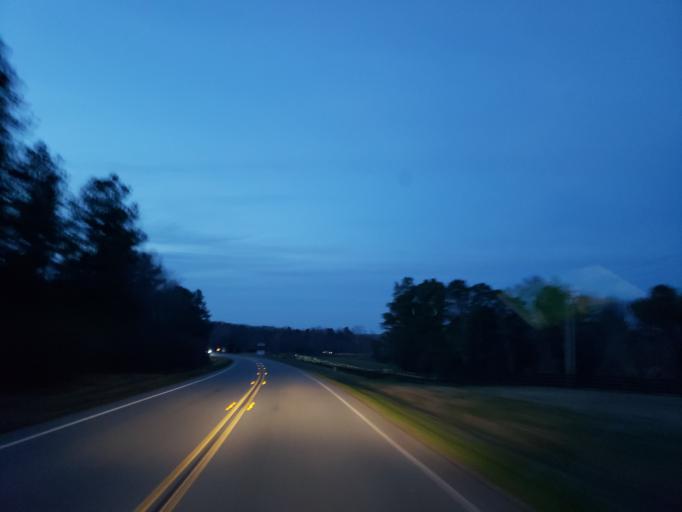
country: US
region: Georgia
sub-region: Pickens County
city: Nelson
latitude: 34.3467
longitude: -84.2647
